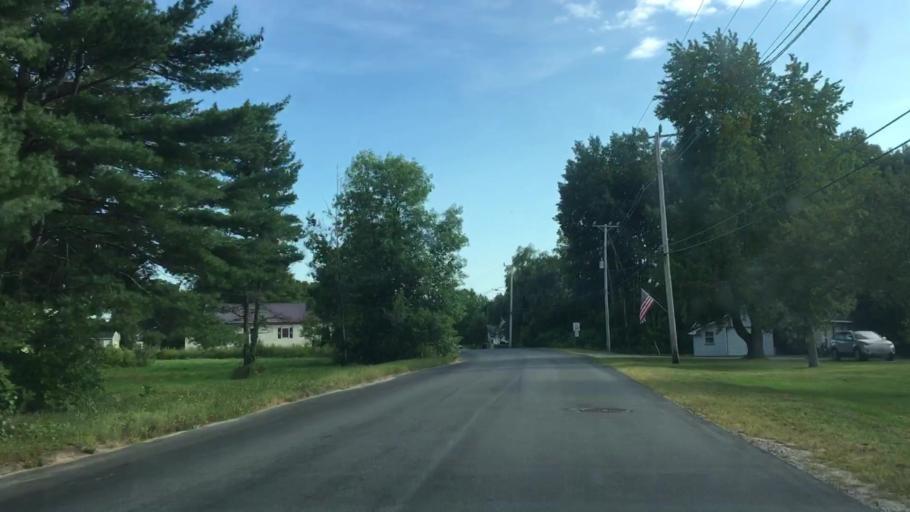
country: US
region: Maine
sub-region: Penobscot County
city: Howland
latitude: 45.2323
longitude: -68.6492
